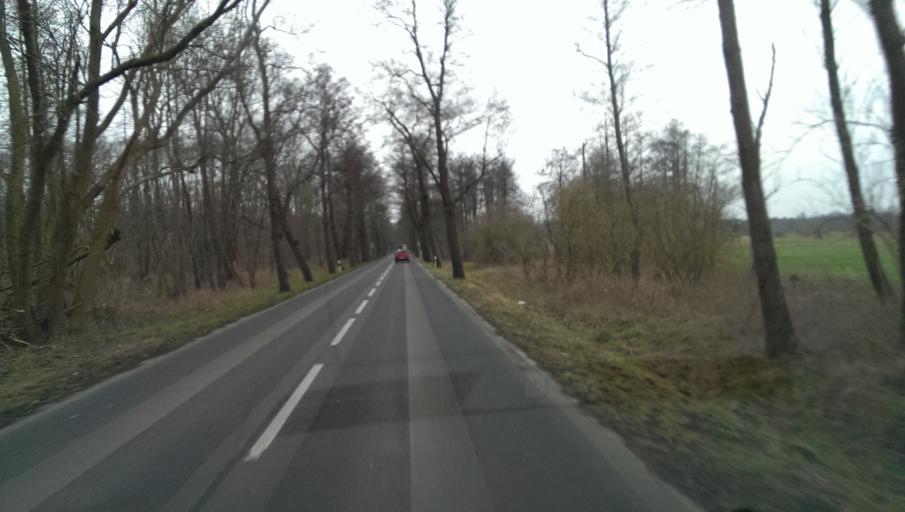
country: DE
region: Brandenburg
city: Grossbeeren
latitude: 52.3432
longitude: 13.3017
